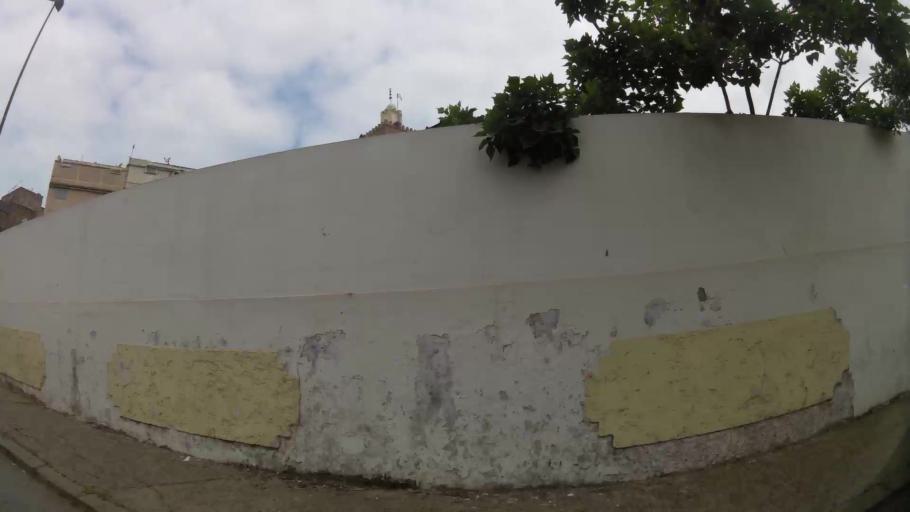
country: MA
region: Rabat-Sale-Zemmour-Zaer
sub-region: Rabat
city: Rabat
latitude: 33.9926
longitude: -6.8736
